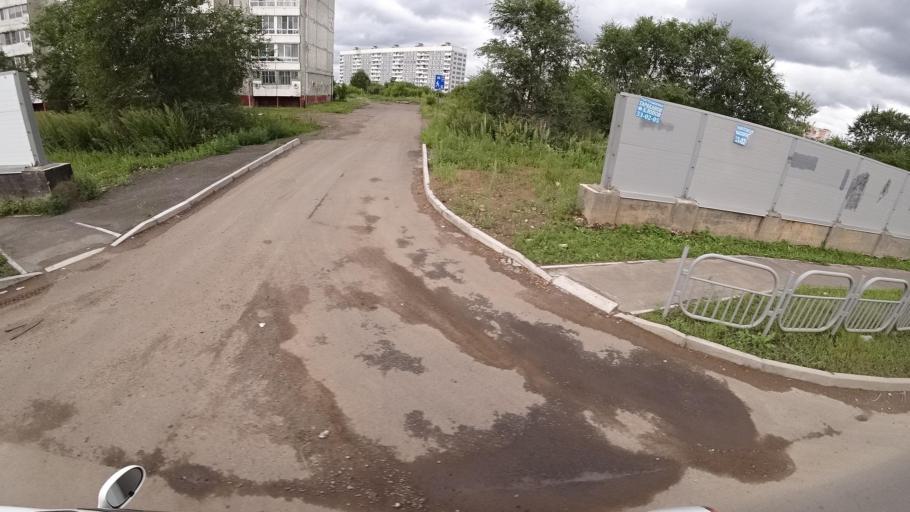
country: RU
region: Khabarovsk Krai
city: Solnechnyy
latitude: 50.5928
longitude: 137.0358
